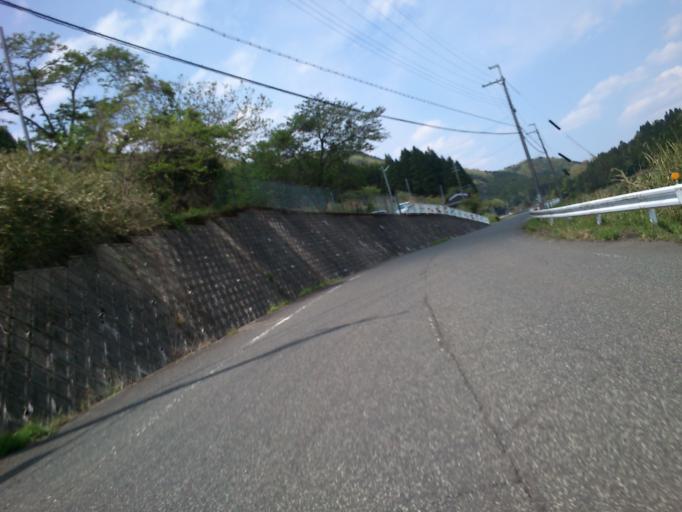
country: JP
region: Kyoto
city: Fukuchiyama
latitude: 35.3831
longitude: 134.9396
